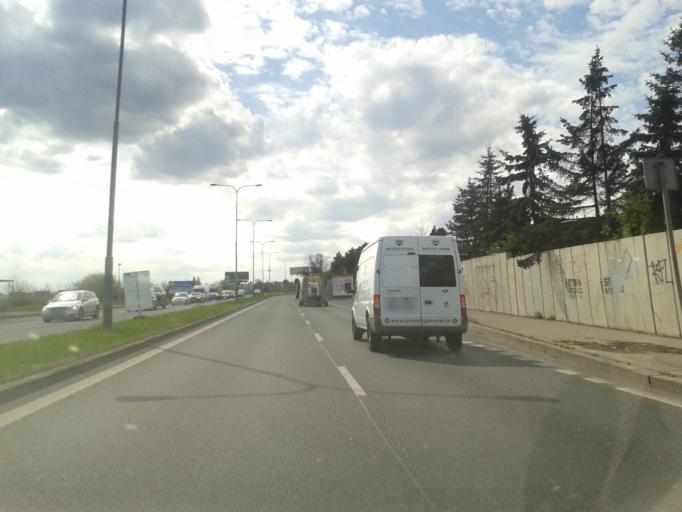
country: CZ
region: Praha
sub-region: Praha 12
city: Modrany
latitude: 50.0270
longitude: 14.3744
